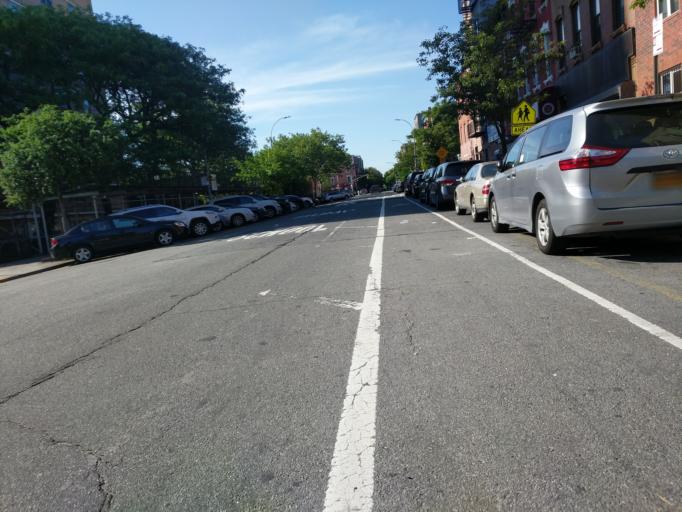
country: US
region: New York
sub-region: Queens County
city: Long Island City
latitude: 40.7059
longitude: -73.9447
